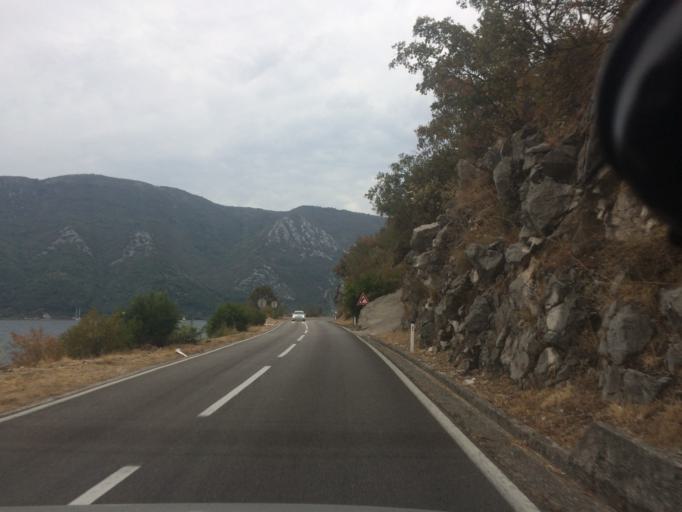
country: ME
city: Lipci
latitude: 42.5019
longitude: 18.6643
